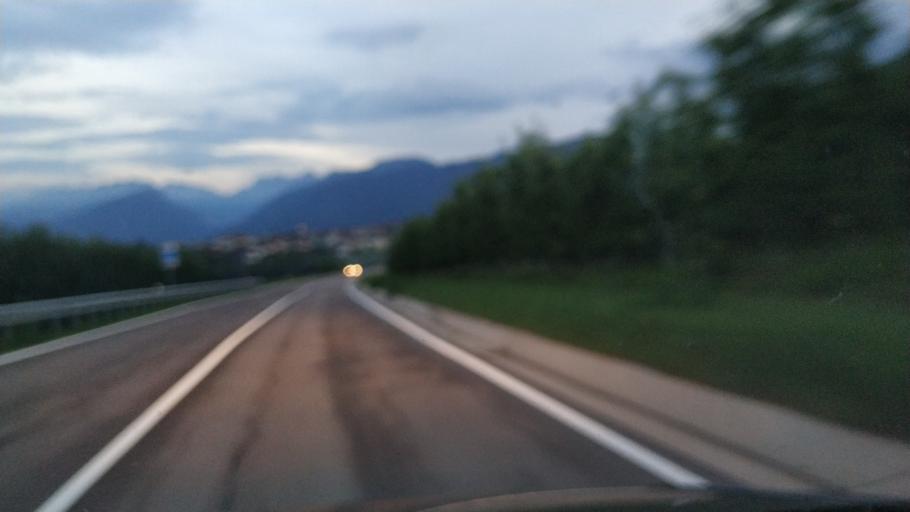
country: IT
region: Trentino-Alto Adige
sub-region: Provincia di Trento
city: Romallo
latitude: 46.4048
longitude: 11.0754
